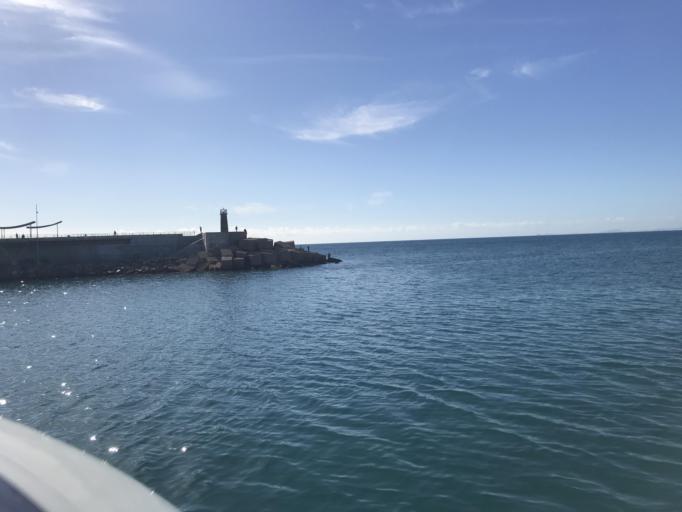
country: ES
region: Valencia
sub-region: Provincia de Alicante
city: Torrevieja
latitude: 37.9657
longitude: -0.6880
